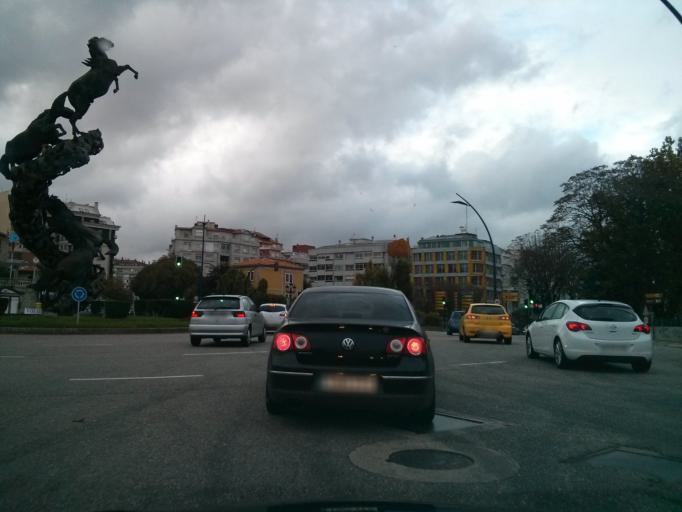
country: ES
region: Galicia
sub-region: Provincia de Pontevedra
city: Vigo
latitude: 42.2291
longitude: -8.7192
